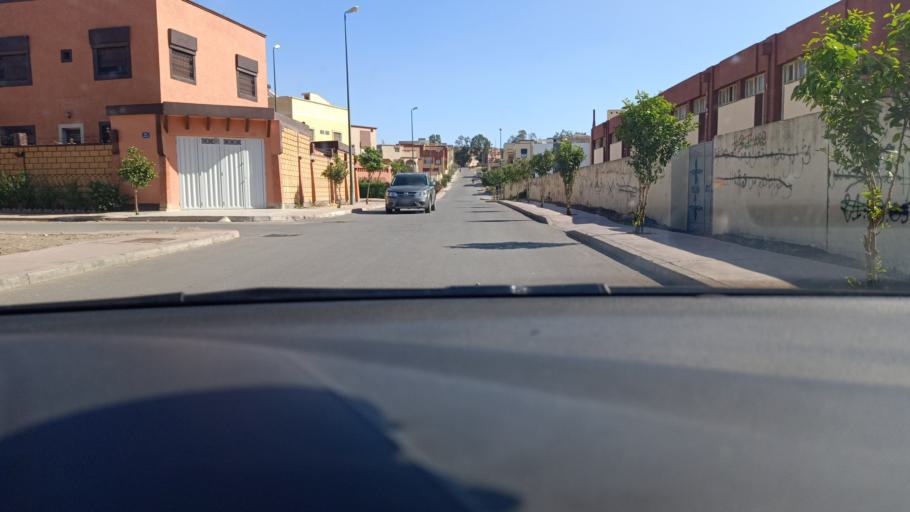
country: MA
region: Doukkala-Abda
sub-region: Safi
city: Youssoufia
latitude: 32.2426
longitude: -8.5329
